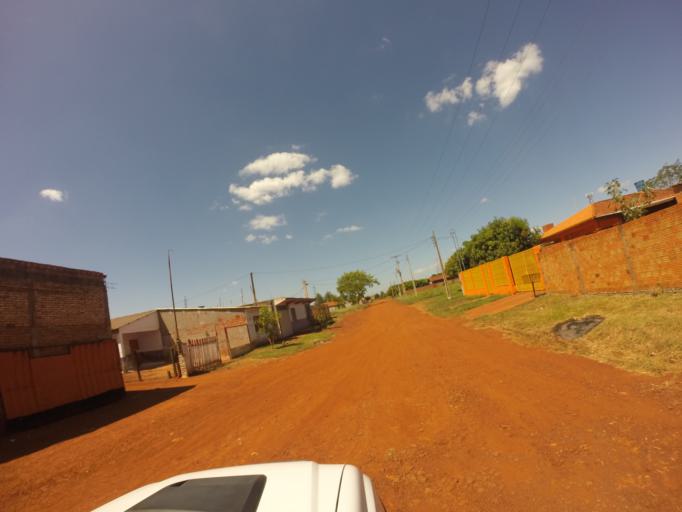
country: PY
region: Alto Parana
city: Ciudad del Este
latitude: -25.4324
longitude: -54.6494
